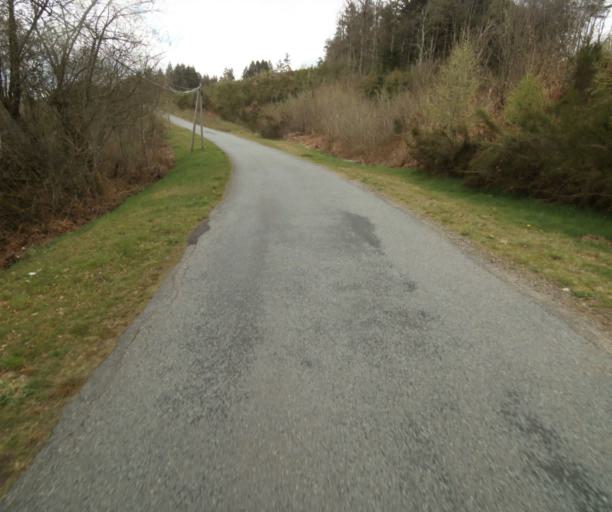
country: FR
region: Limousin
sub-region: Departement de la Correze
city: Correze
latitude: 45.3193
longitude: 1.9359
